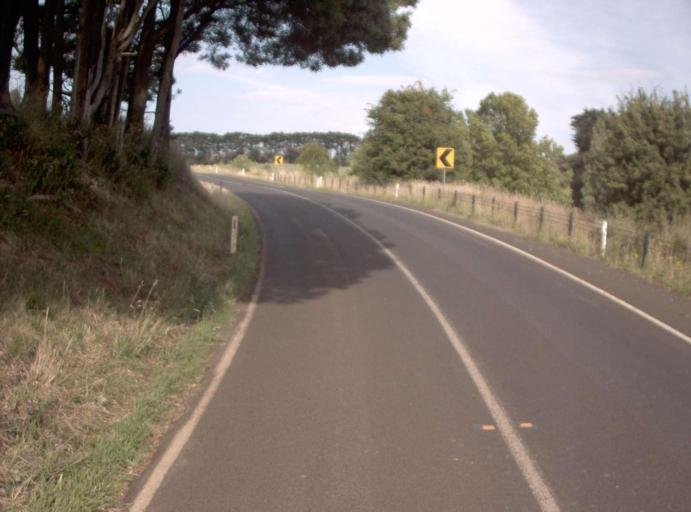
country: AU
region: Victoria
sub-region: Latrobe
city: Moe
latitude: -38.2836
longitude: 146.1992
